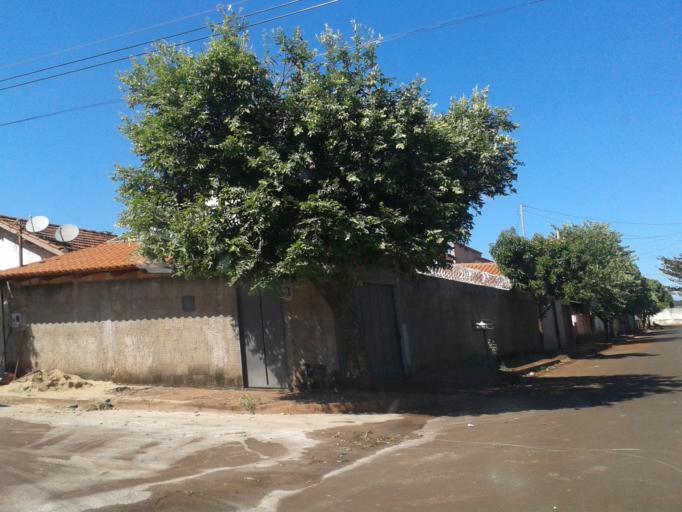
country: BR
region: Minas Gerais
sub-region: Centralina
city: Centralina
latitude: -18.5953
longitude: -49.1950
